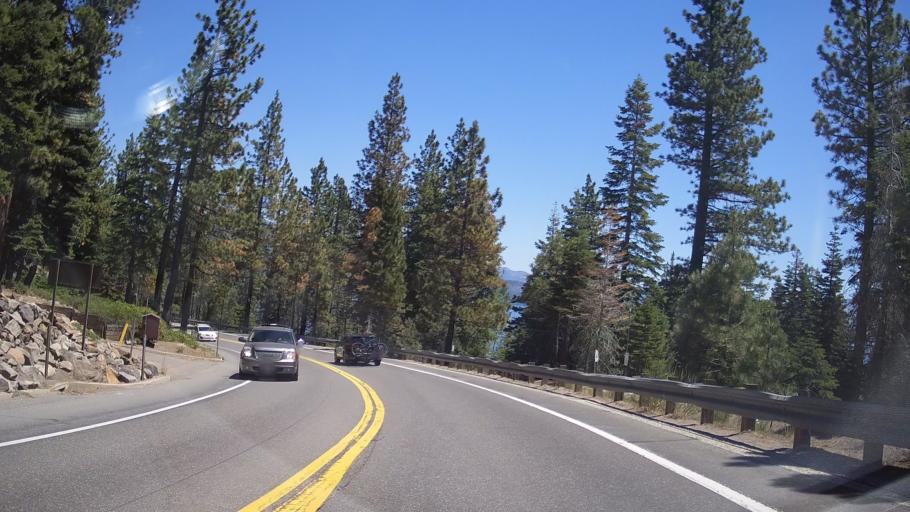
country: US
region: California
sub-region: Placer County
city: Dollar Point
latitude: 39.1985
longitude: -120.0972
